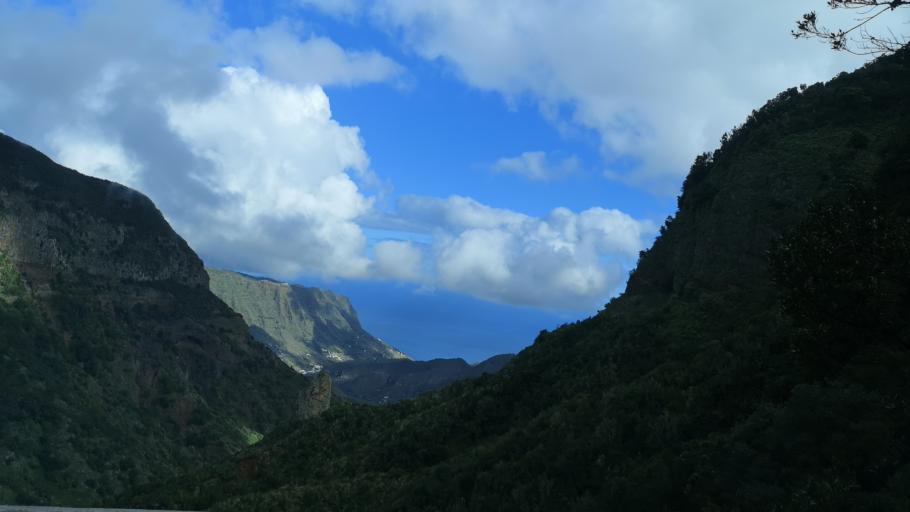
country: ES
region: Canary Islands
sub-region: Provincia de Santa Cruz de Tenerife
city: Hermigua
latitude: 28.1251
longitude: -17.2058
